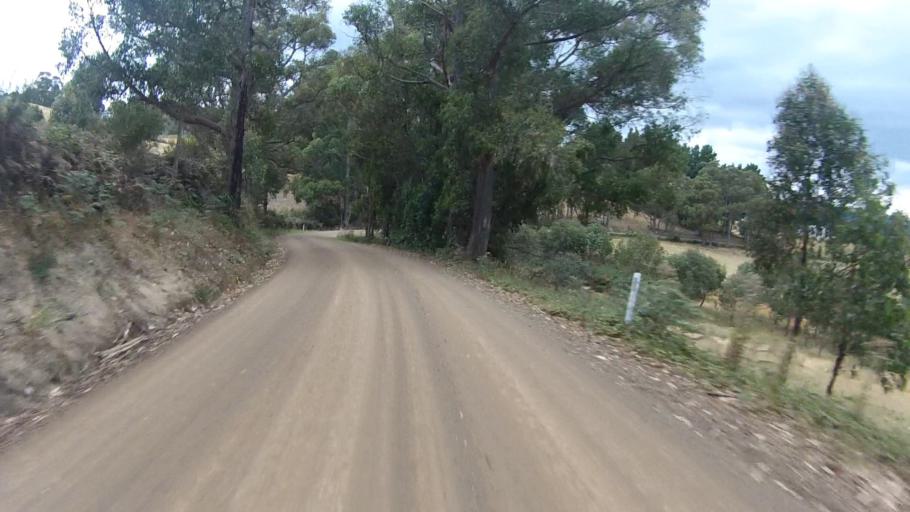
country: AU
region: Tasmania
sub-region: Huon Valley
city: Huonville
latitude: -42.9709
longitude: 147.0605
